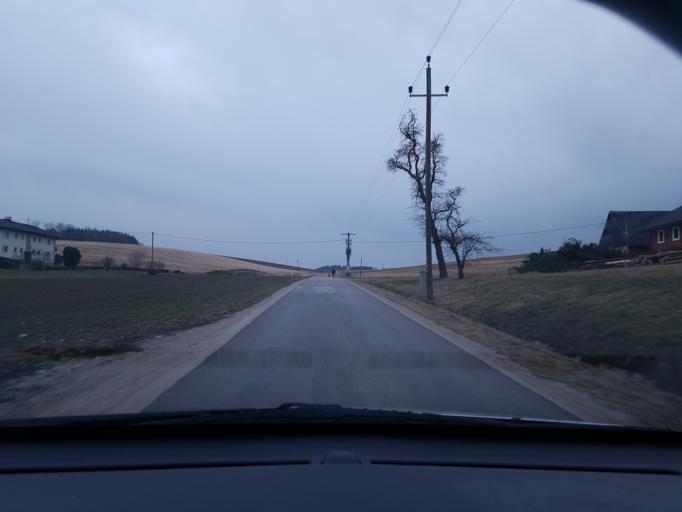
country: AT
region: Upper Austria
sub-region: Politischer Bezirk Linz-Land
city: Ansfelden
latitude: 48.1578
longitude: 14.3308
